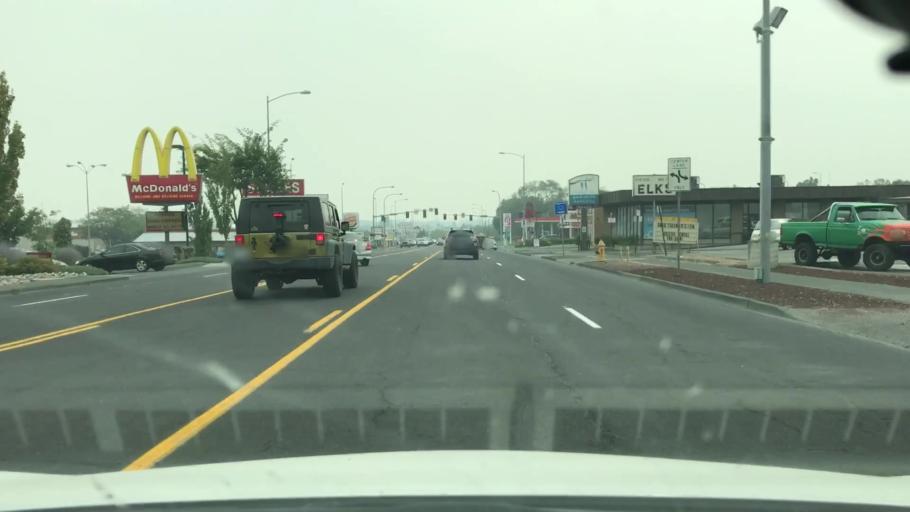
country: US
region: Washington
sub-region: Grant County
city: Moses Lake
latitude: 47.1401
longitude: -119.2784
